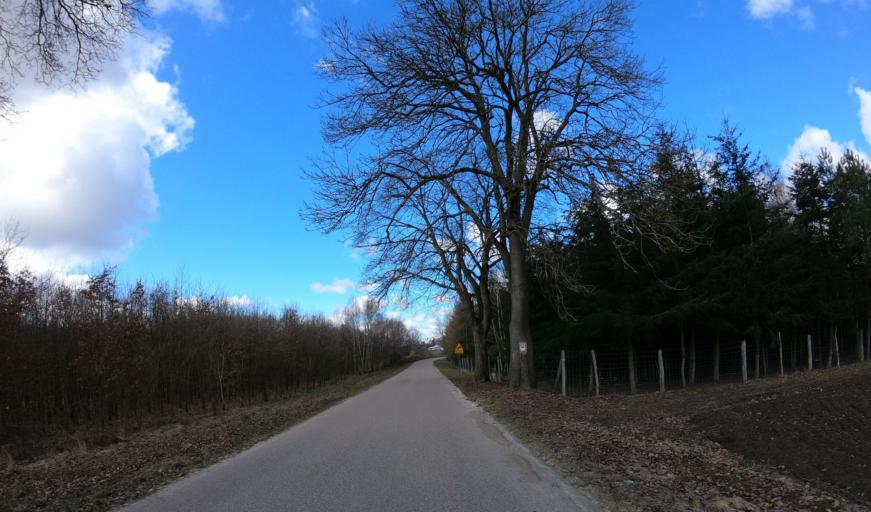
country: PL
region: West Pomeranian Voivodeship
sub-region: Powiat drawski
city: Zlocieniec
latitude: 53.4830
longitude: 15.9147
